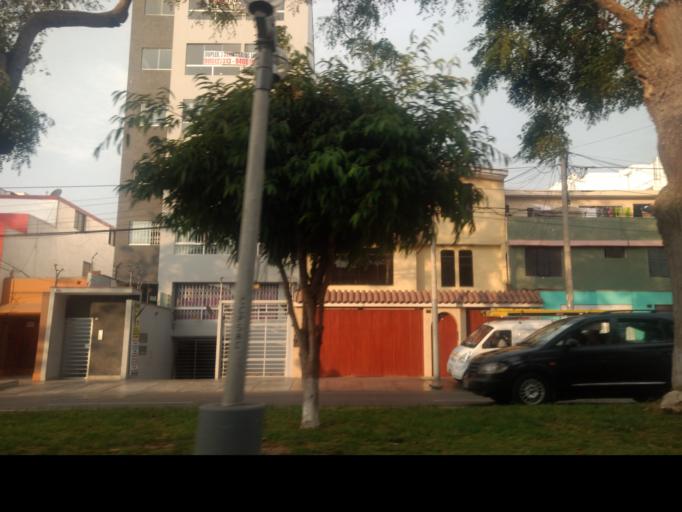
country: PE
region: Callao
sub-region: Callao
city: Callao
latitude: -12.0749
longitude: -77.1026
